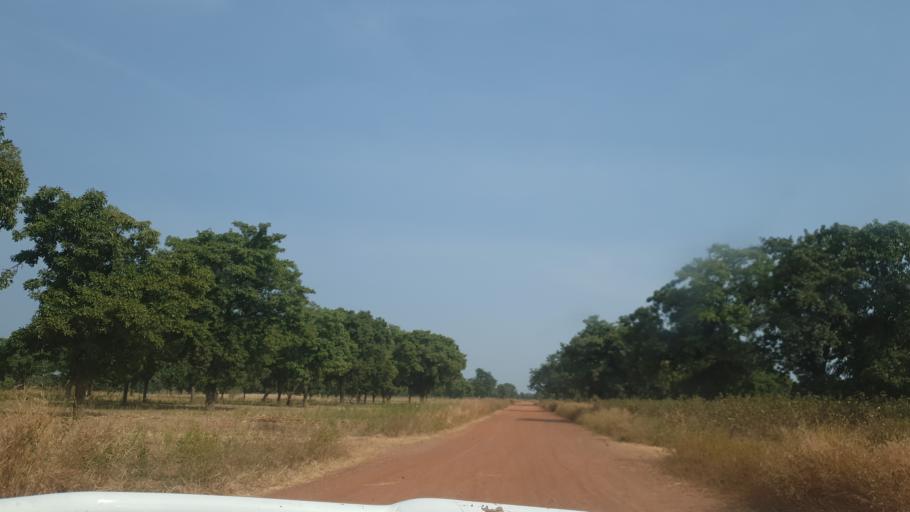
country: ML
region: Koulikoro
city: Dioila
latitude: 12.2301
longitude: -6.2249
